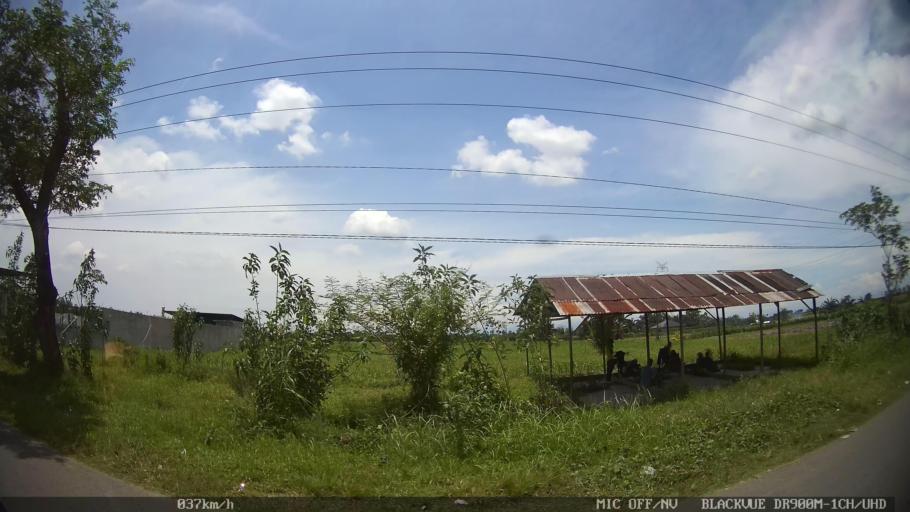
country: ID
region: North Sumatra
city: Binjai
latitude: 3.5912
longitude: 98.5155
